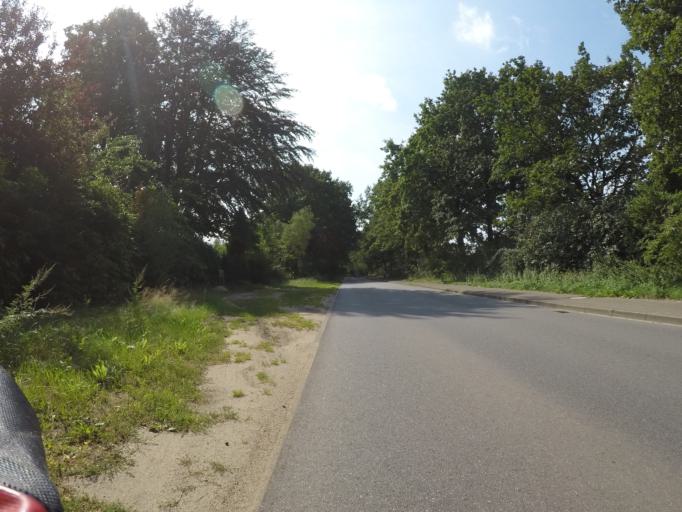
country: DE
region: Schleswig-Holstein
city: Tangstedt
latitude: 53.7076
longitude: 10.0564
